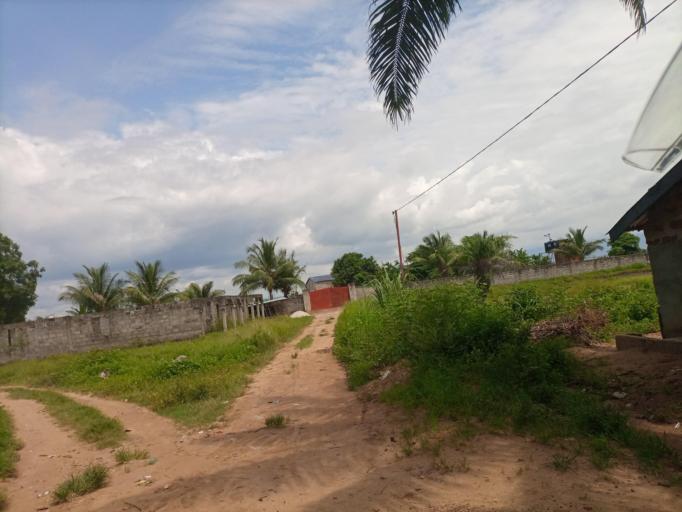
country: SL
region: Western Area
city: Freetown
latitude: 8.5257
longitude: -13.1432
